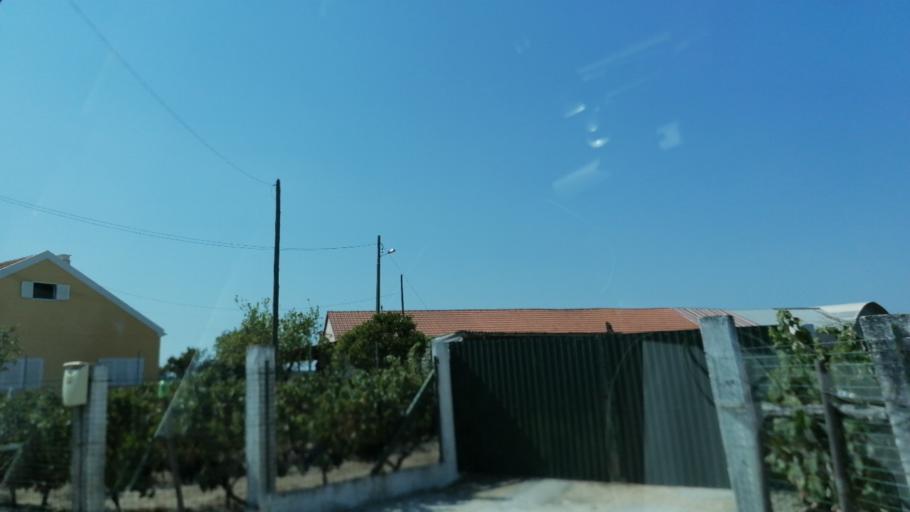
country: PT
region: Santarem
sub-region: Benavente
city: Poceirao
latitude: 38.7502
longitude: -8.6619
